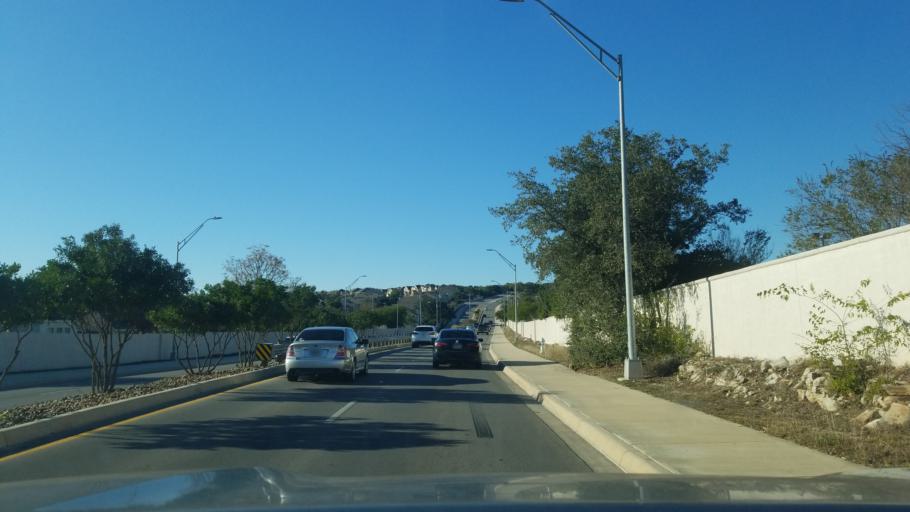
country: US
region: Texas
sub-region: Bexar County
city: Hollywood Park
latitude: 29.6368
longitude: -98.4855
